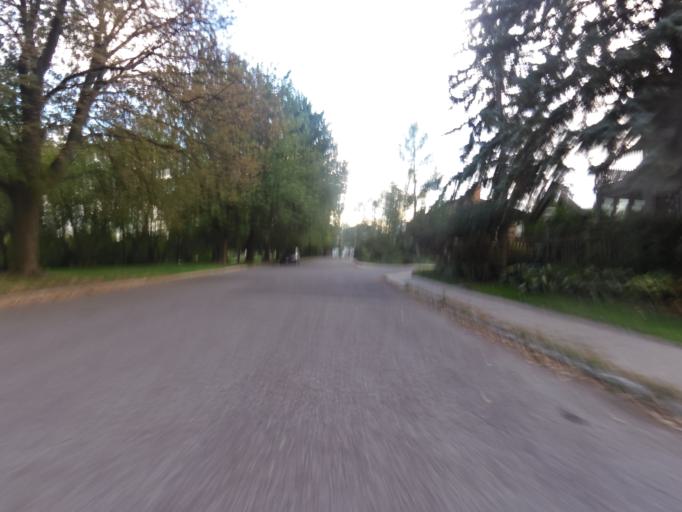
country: CA
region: Ontario
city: Ottawa
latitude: 45.3982
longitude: -75.6734
